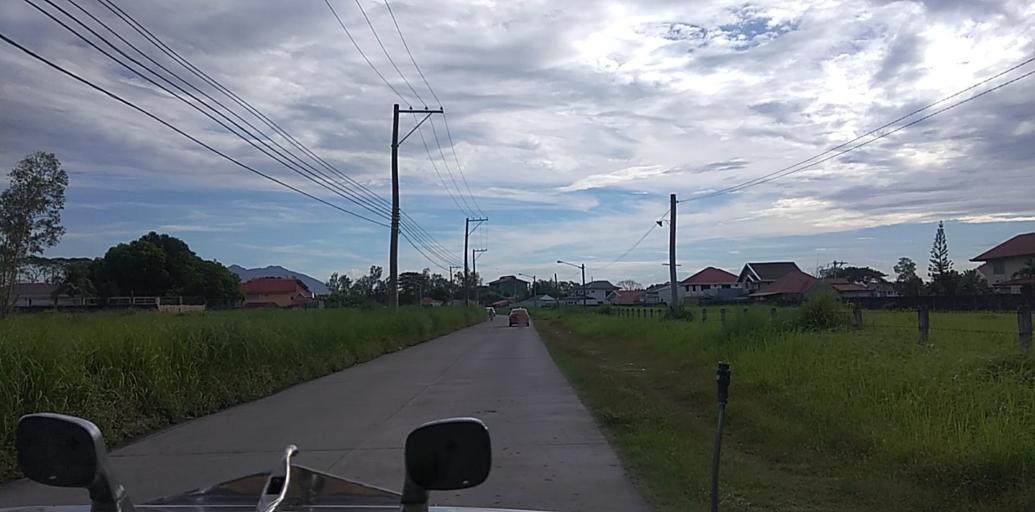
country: PH
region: Central Luzon
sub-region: Province of Pampanga
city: Telabastagan
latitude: 15.1061
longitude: 120.6083
